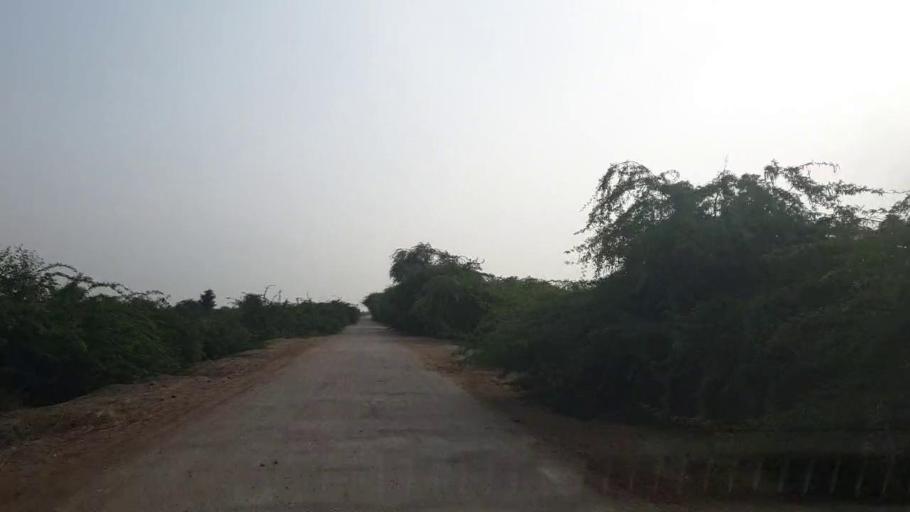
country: PK
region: Sindh
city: Badin
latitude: 24.6354
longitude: 68.6925
